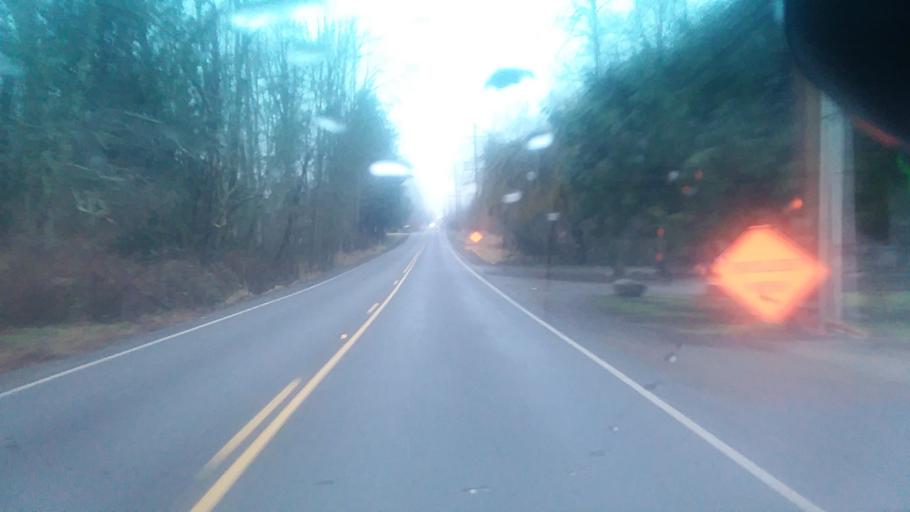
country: US
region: Washington
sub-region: Pierce County
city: South Hill
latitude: 47.1257
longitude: -122.3079
